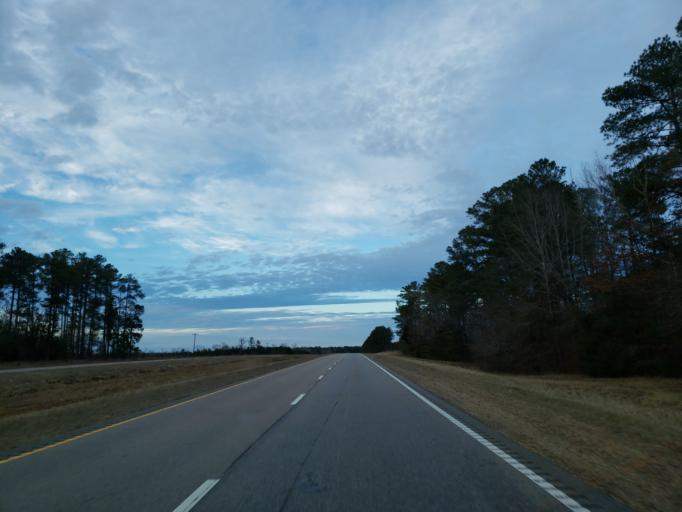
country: US
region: Mississippi
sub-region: Kemper County
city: De Kalb
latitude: 32.7102
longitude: -88.4813
